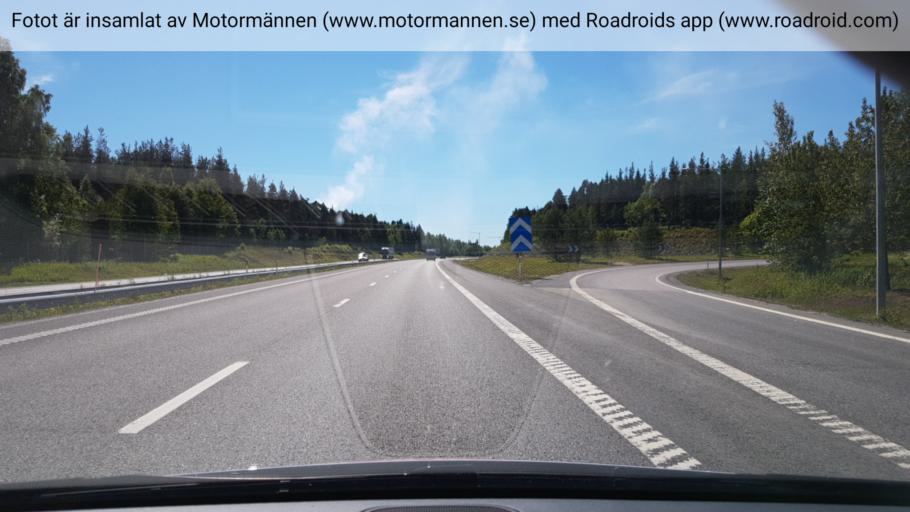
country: SE
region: Norrbotten
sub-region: Pitea Kommun
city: Pitea
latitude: 65.3320
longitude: 21.4414
